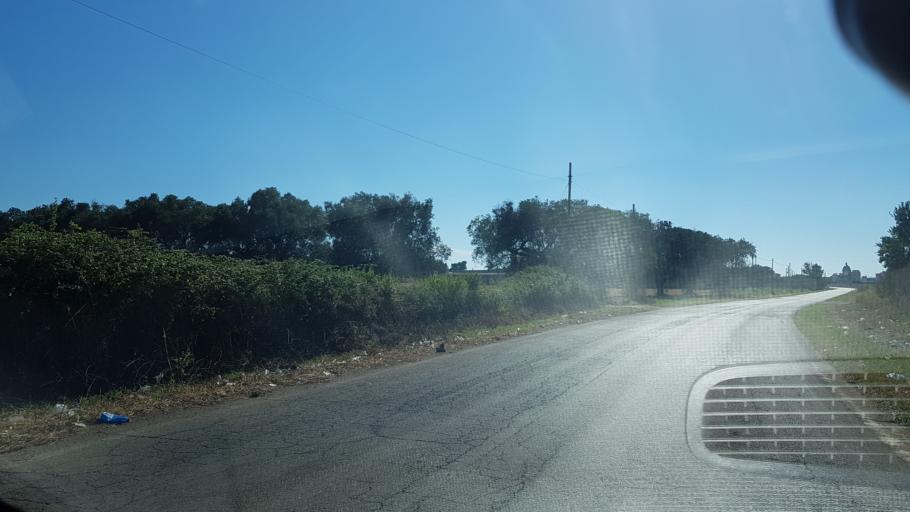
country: IT
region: Apulia
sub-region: Provincia di Brindisi
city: Mesagne
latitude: 40.5576
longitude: 17.8325
